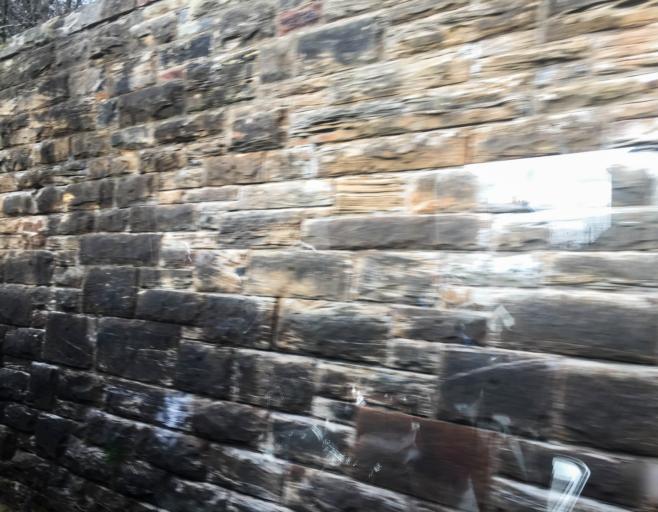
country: GB
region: Scotland
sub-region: North Lanarkshire
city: Wishaw
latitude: 55.7776
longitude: -3.9395
